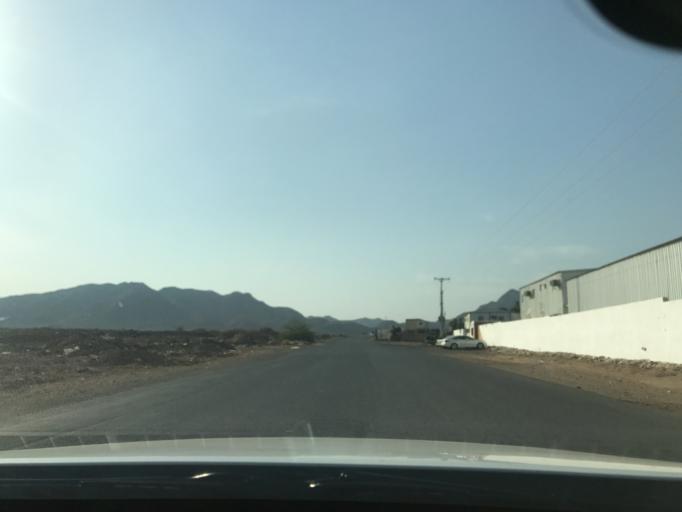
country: SA
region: Makkah
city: Al Jumum
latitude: 21.4383
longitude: 39.5186
